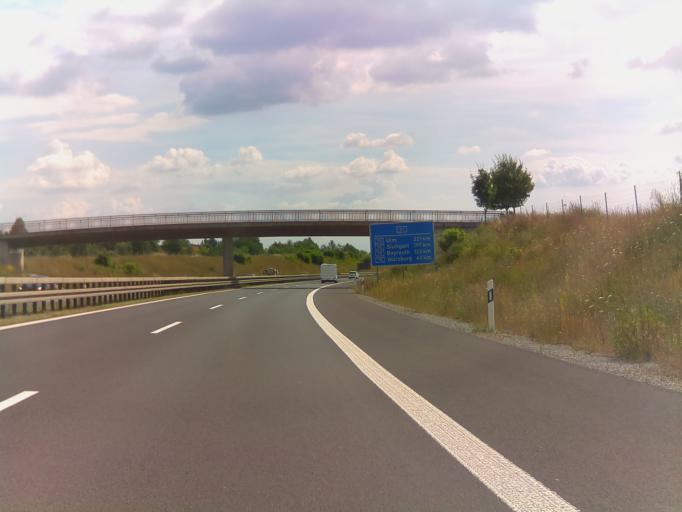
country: DE
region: Bavaria
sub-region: Regierungsbezirk Unterfranken
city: Geldersheim
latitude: 50.0534
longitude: 10.1499
